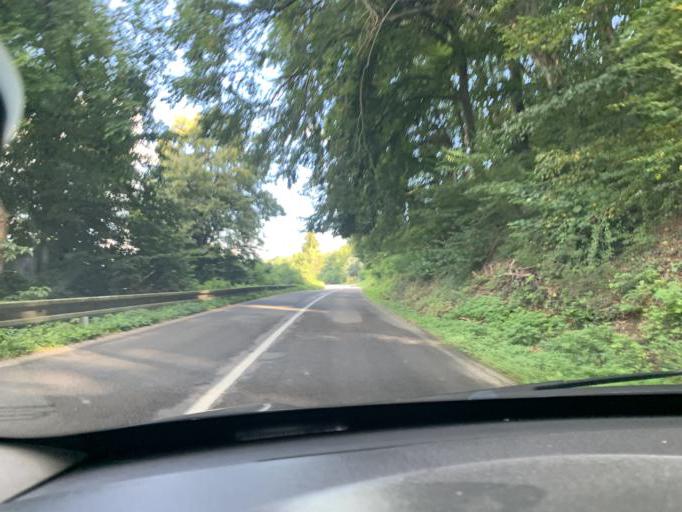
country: SK
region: Trenciansky
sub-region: Okres Trencin
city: Trencin
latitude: 48.8282
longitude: 17.9505
